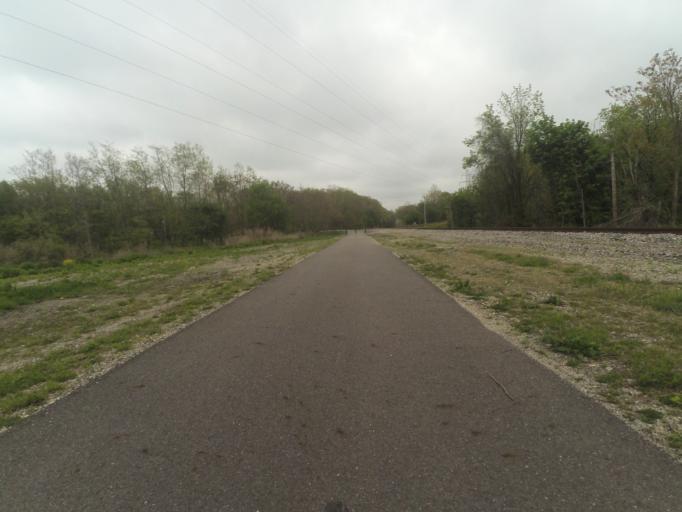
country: US
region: Ohio
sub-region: Portage County
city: Kent
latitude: 41.1719
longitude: -81.3138
